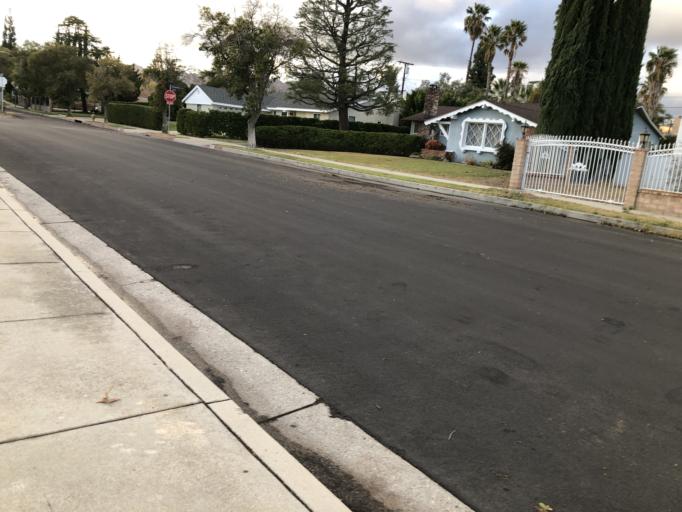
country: US
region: California
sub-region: Los Angeles County
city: Chatsworth
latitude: 34.2627
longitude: -118.5859
